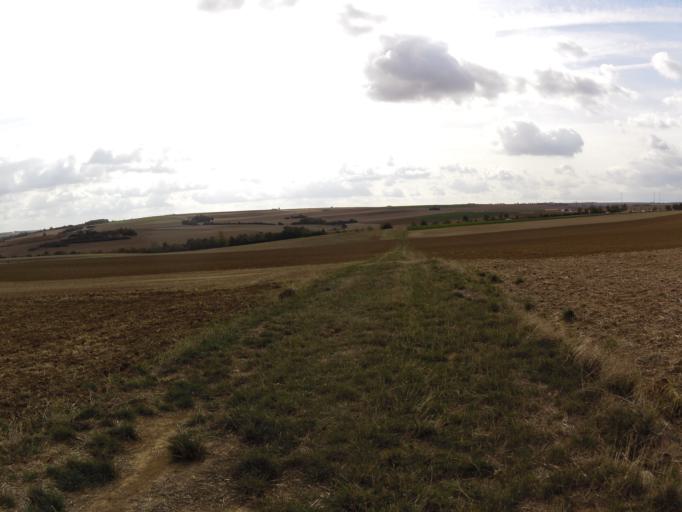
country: DE
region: Bavaria
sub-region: Regierungsbezirk Unterfranken
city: Reichenberg
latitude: 49.7354
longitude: 9.9377
